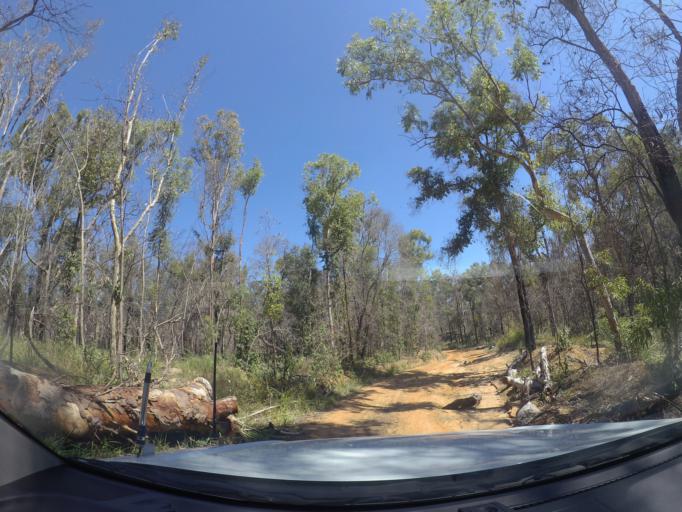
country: AU
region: Queensland
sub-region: Logan
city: North Maclean
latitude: -27.7795
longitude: 152.9367
